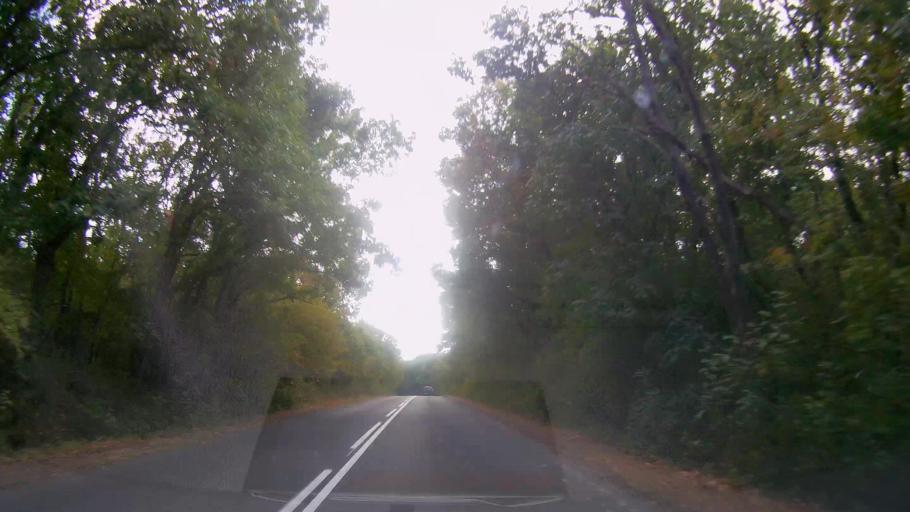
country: BG
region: Burgas
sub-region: Obshtina Primorsko
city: Primorsko
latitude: 42.2955
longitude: 27.7298
